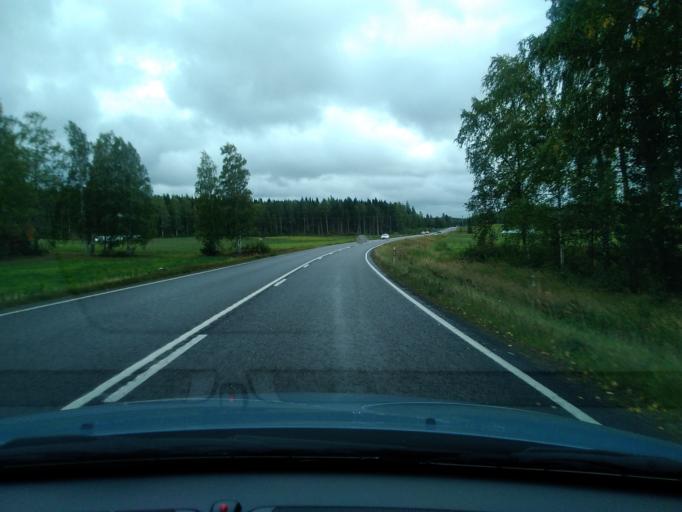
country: FI
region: Central Finland
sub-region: Saarijaervi-Viitasaari
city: Saarijaervi
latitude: 62.6884
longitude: 25.3279
